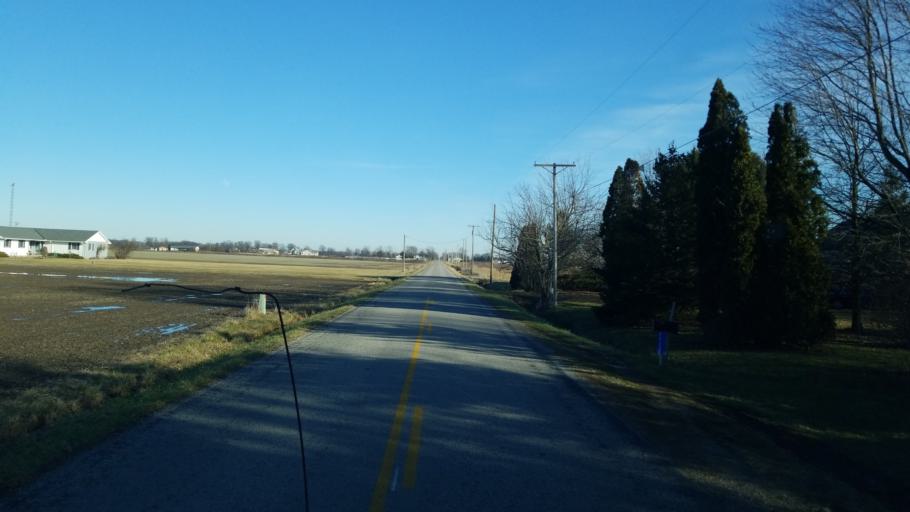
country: US
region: Ohio
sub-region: Sandusky County
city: Mount Carmel
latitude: 41.2561
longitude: -82.9535
